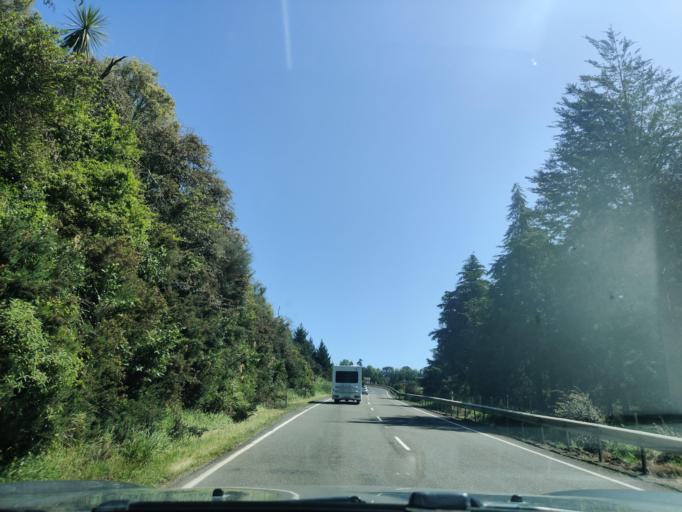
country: NZ
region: Manawatu-Wanganui
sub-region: Wanganui District
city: Wanganui
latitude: -39.8445
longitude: 174.9249
